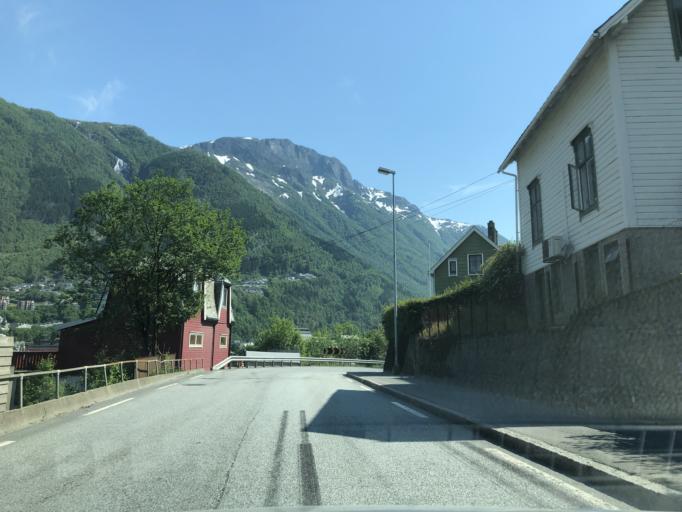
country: NO
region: Hordaland
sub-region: Odda
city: Odda
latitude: 60.0727
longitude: 6.5389
